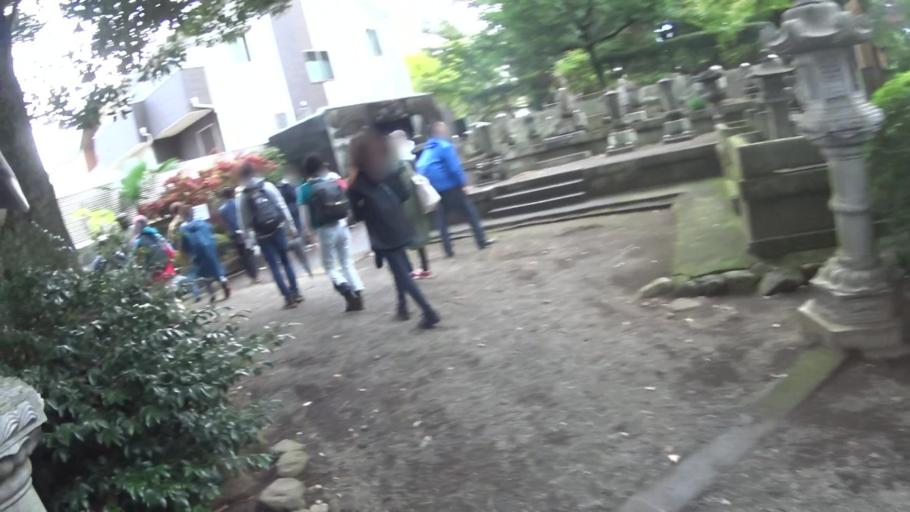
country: JP
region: Kanagawa
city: Hadano
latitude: 35.3708
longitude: 139.2138
